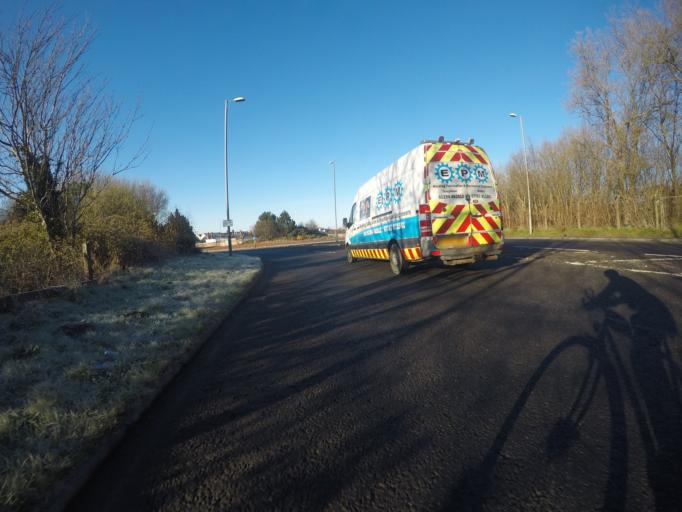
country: GB
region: Scotland
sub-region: North Ayrshire
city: Stevenston
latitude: 55.6348
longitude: -4.7433
